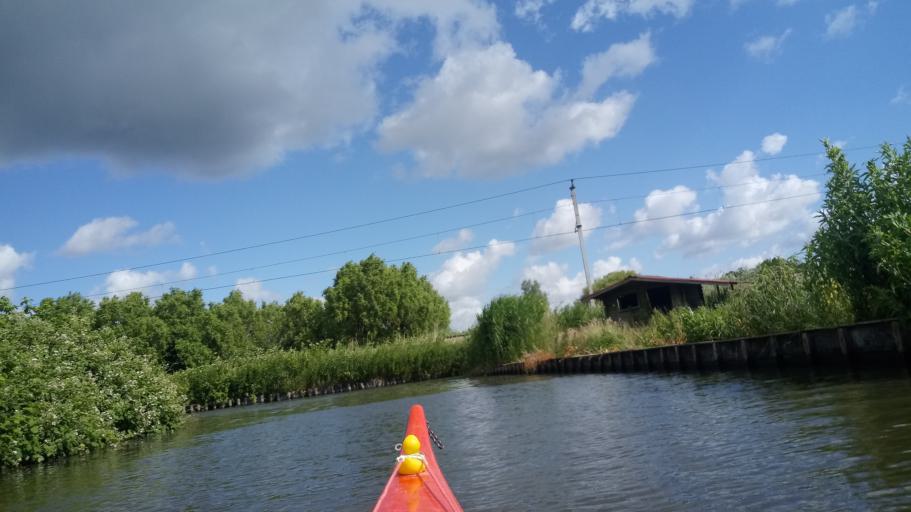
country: NL
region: North Holland
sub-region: Gemeente Enkhuizen
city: Enkhuizen
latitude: 52.6950
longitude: 5.2139
